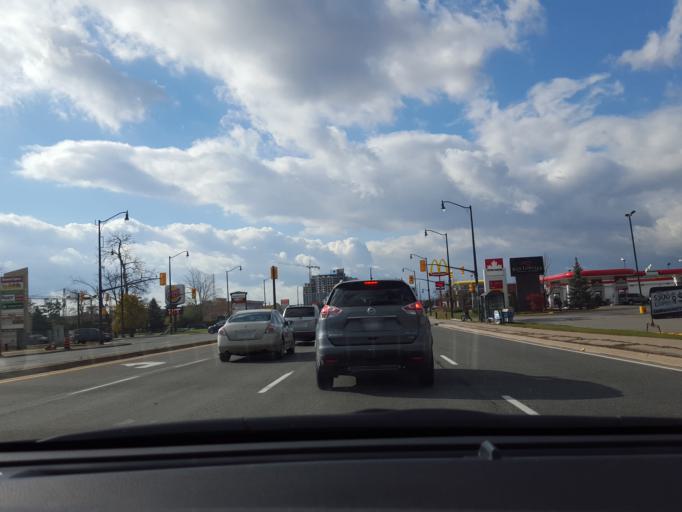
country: CA
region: Ontario
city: Brampton
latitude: 43.7042
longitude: -79.7399
